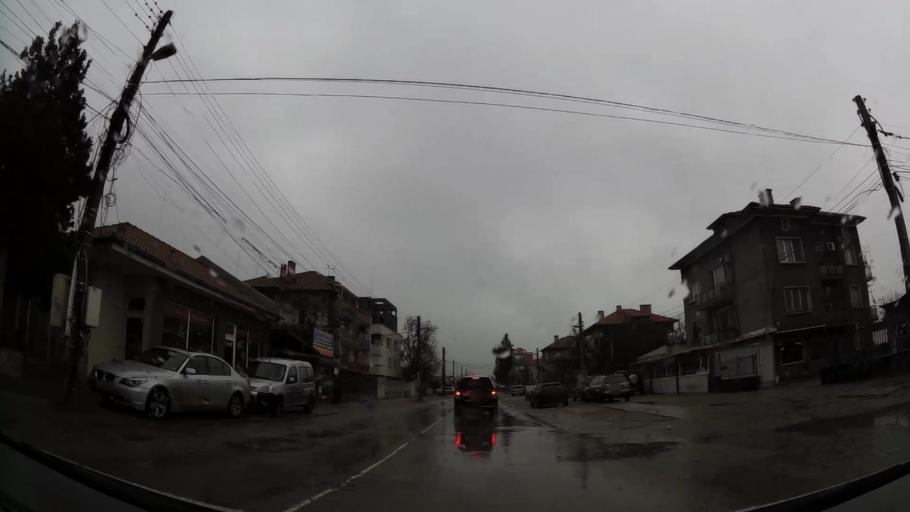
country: BG
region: Sofia-Capital
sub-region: Stolichna Obshtina
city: Sofia
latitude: 42.6359
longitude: 23.4105
